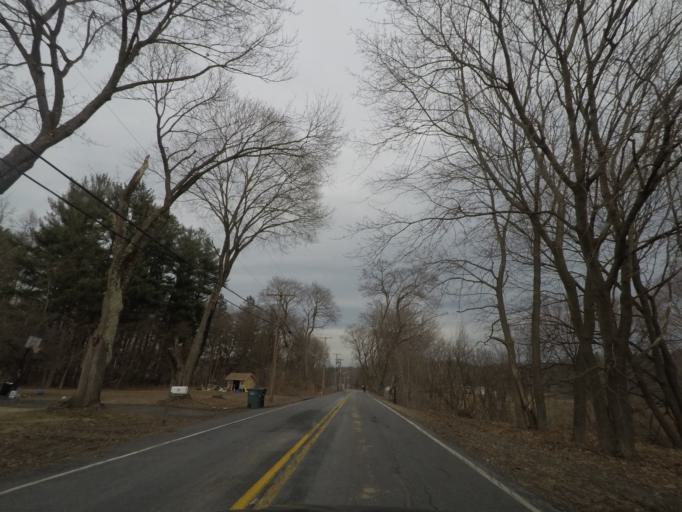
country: US
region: New York
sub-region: Saratoga County
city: Schuylerville
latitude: 43.1172
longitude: -73.5707
